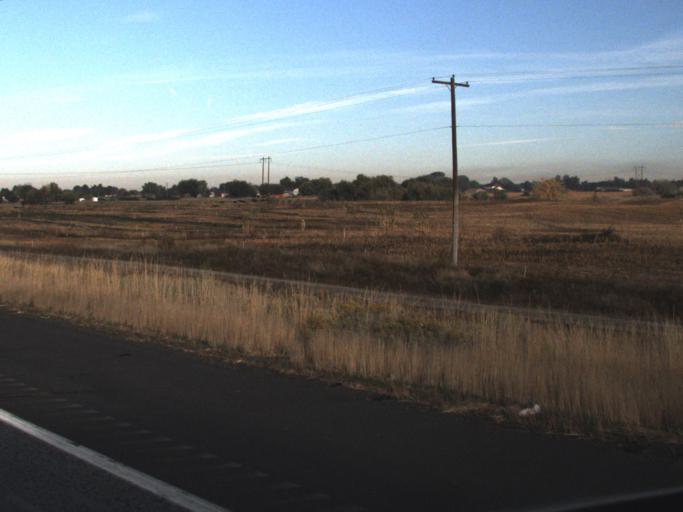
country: US
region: Washington
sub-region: Benton County
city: Prosser
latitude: 46.2214
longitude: -119.7590
